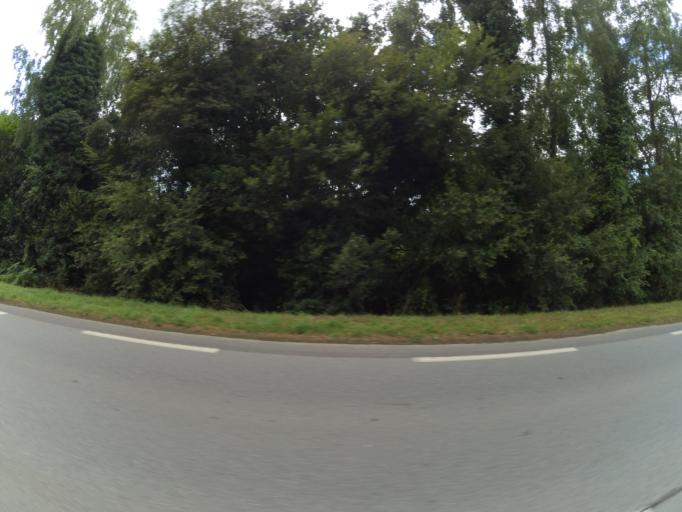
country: FR
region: Brittany
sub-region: Departement du Morbihan
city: Merlevenez
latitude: 47.7477
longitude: -3.2271
